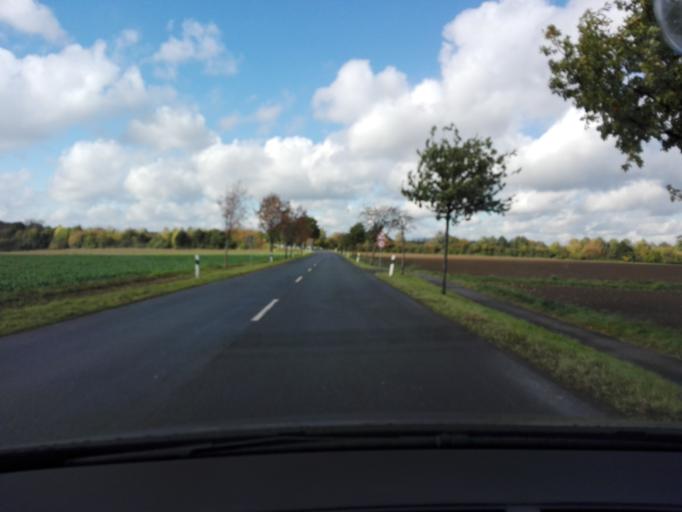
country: DE
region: North Rhine-Westphalia
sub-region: Regierungsbezirk Arnsberg
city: Holzwickede
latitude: 51.5026
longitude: 7.6522
